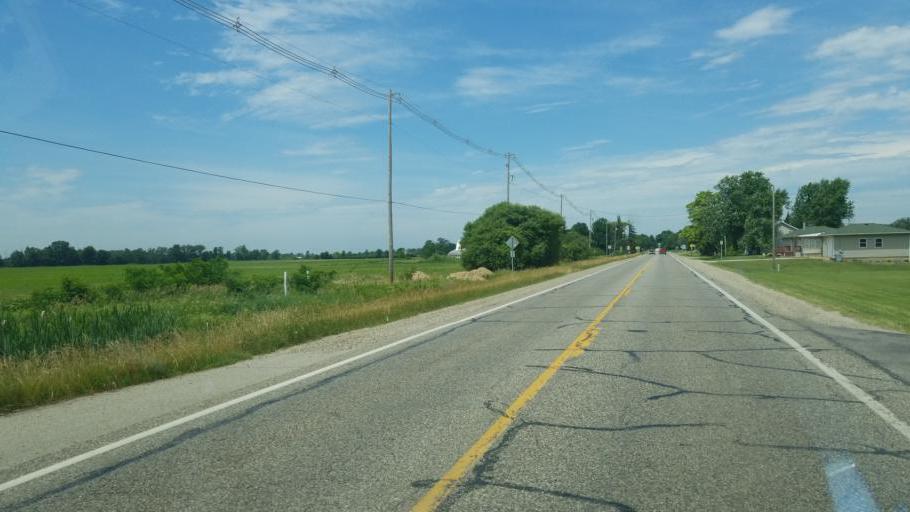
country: US
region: Michigan
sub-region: Eaton County
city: Charlotte
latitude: 42.5647
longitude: -84.8520
